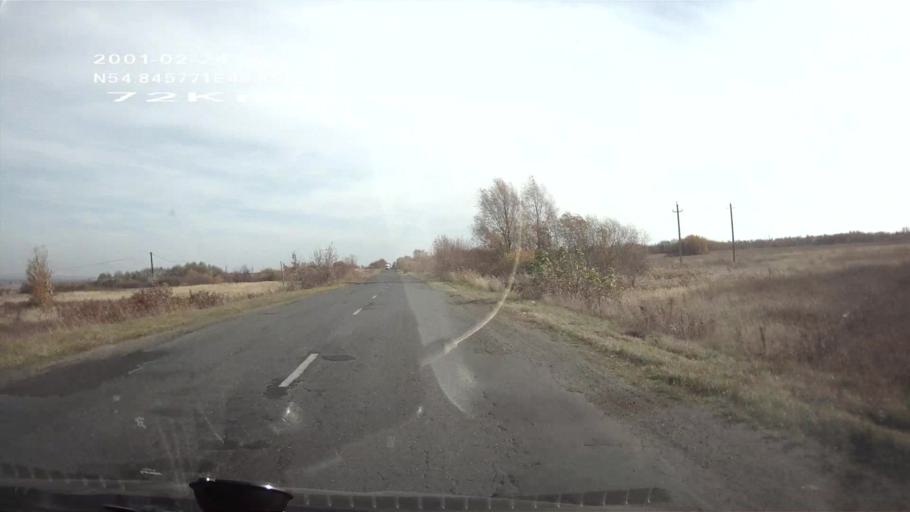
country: RU
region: Chuvashia
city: Alatyr'
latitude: 54.8458
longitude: 46.4565
